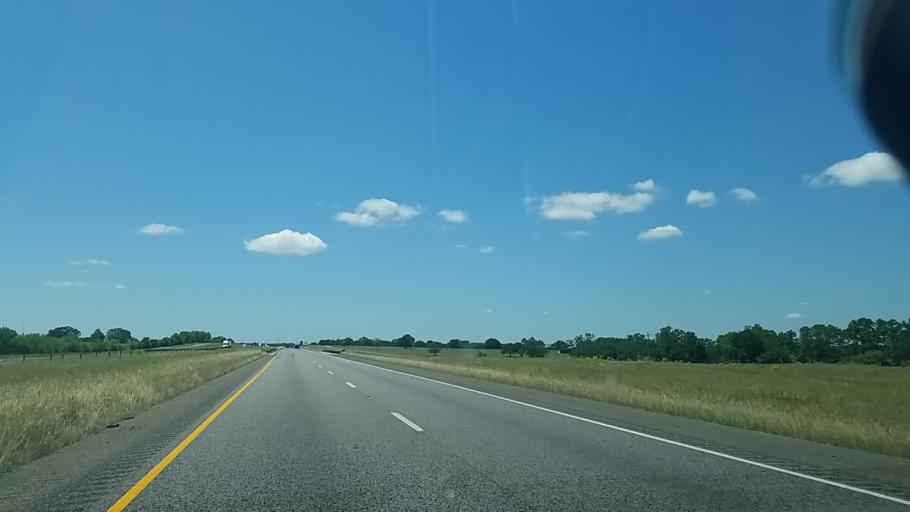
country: US
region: Texas
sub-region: Madison County
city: Madisonville
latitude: 30.9462
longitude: -95.8537
